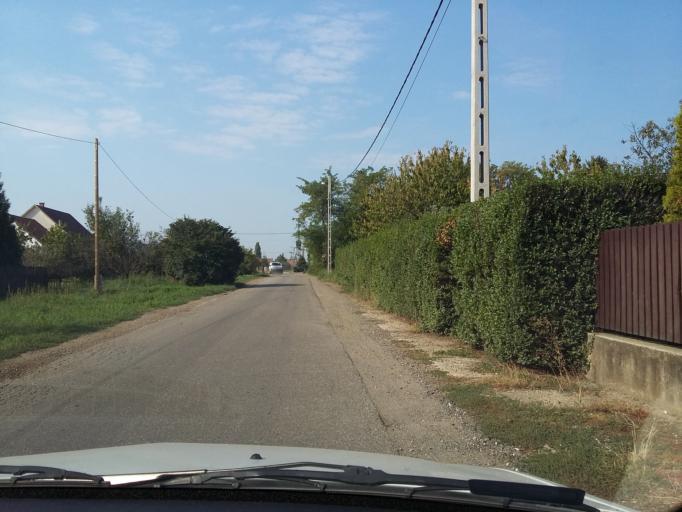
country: HU
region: Borsod-Abauj-Zemplen
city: Bekecs
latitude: 48.1550
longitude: 21.1868
